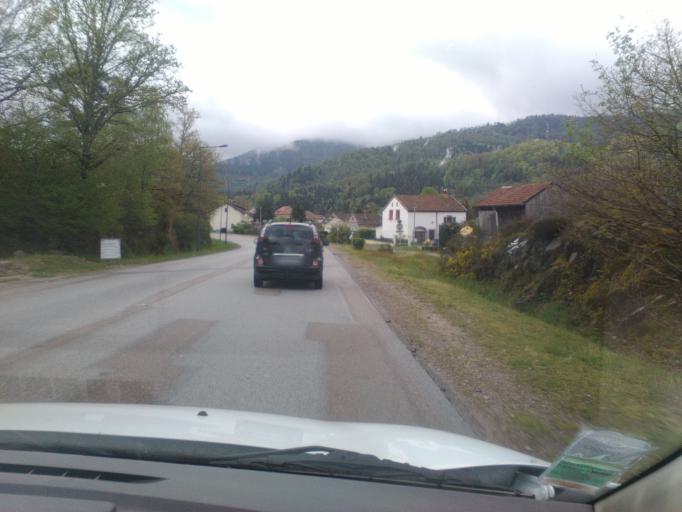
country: FR
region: Lorraine
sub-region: Departement des Vosges
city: Vagney
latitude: 47.9741
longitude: 6.7284
